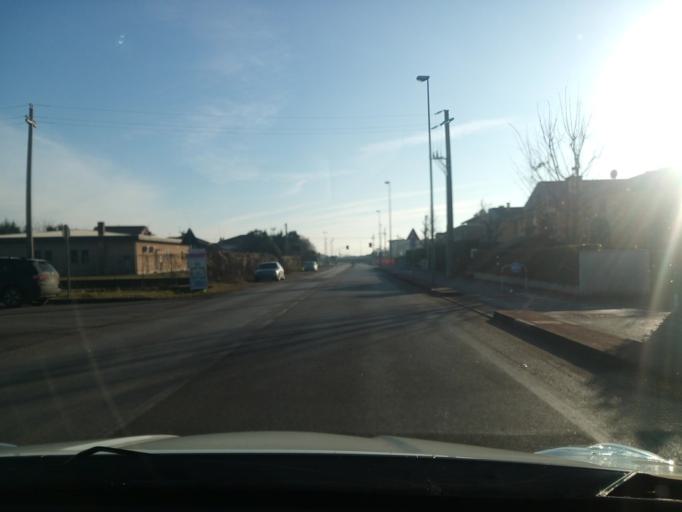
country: IT
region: Veneto
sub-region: Provincia di Vicenza
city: Dueville
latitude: 45.6383
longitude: 11.5571
